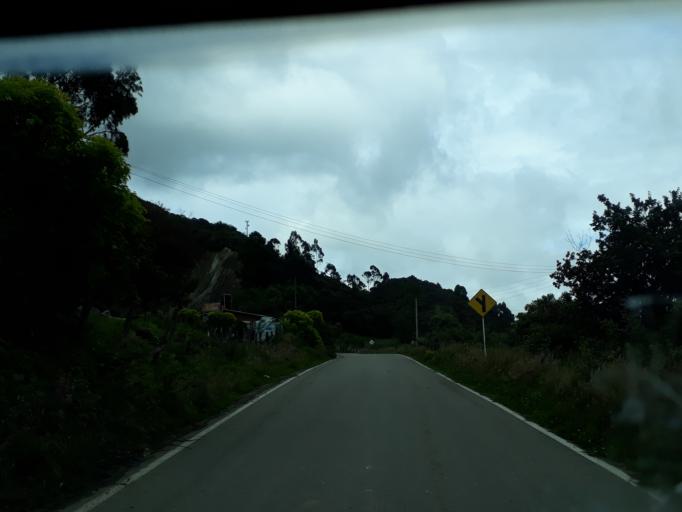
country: CO
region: Cundinamarca
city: La Mesa
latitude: 5.2052
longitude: -73.9023
